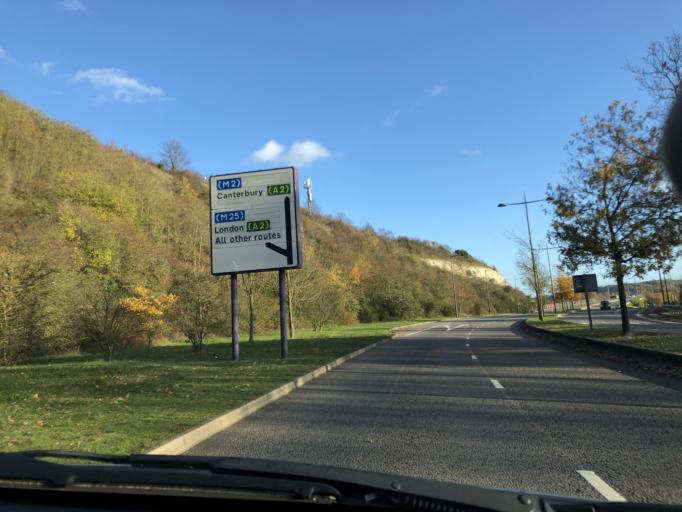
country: GB
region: England
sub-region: Kent
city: Stone
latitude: 51.4432
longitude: 0.2730
